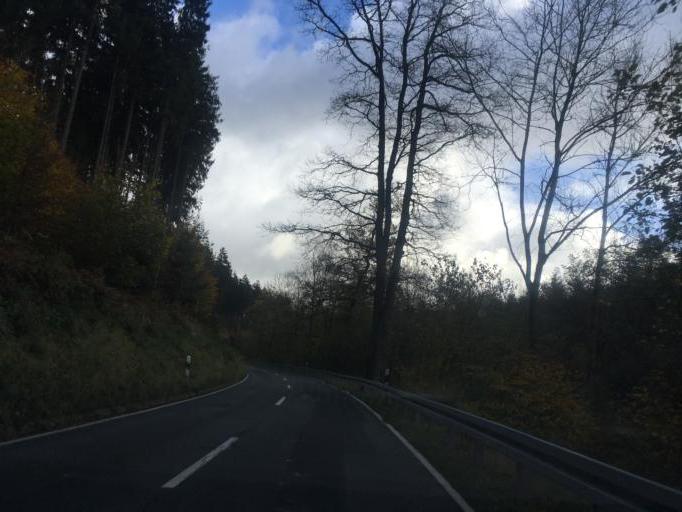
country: DE
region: Lower Saxony
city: Furstenberg
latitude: 51.7558
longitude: 9.4517
